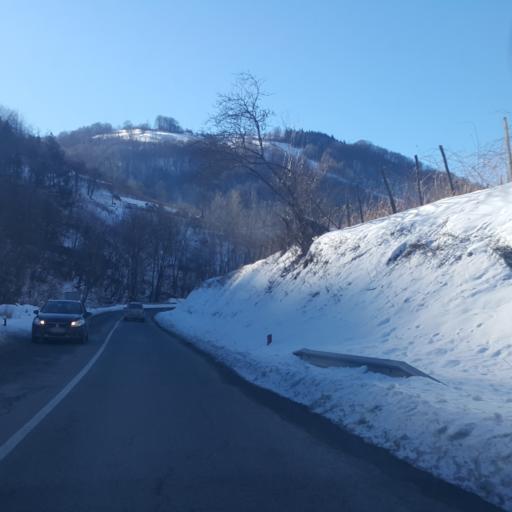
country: RS
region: Central Serbia
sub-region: Rasinski Okrug
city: Aleksandrovac
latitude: 43.3157
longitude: 20.9182
